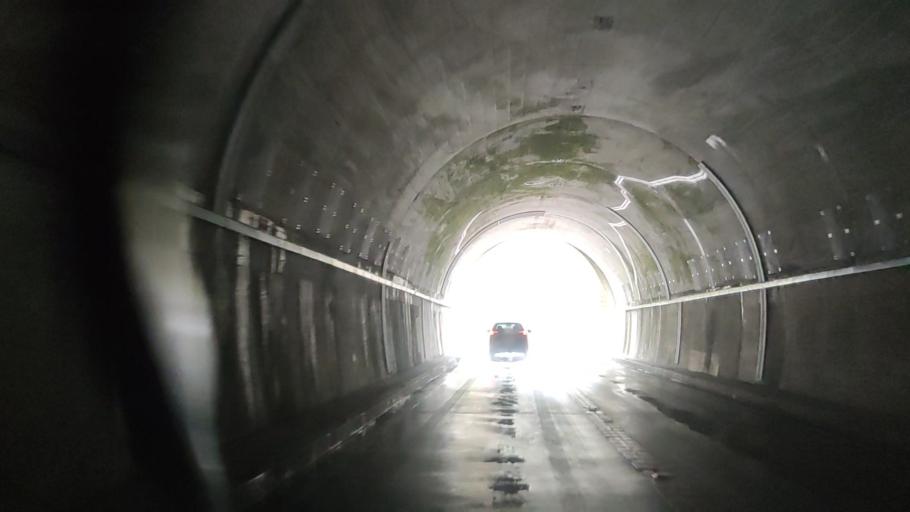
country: JP
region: Tokushima
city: Kamojimacho-jogejima
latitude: 34.1636
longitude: 134.3494
